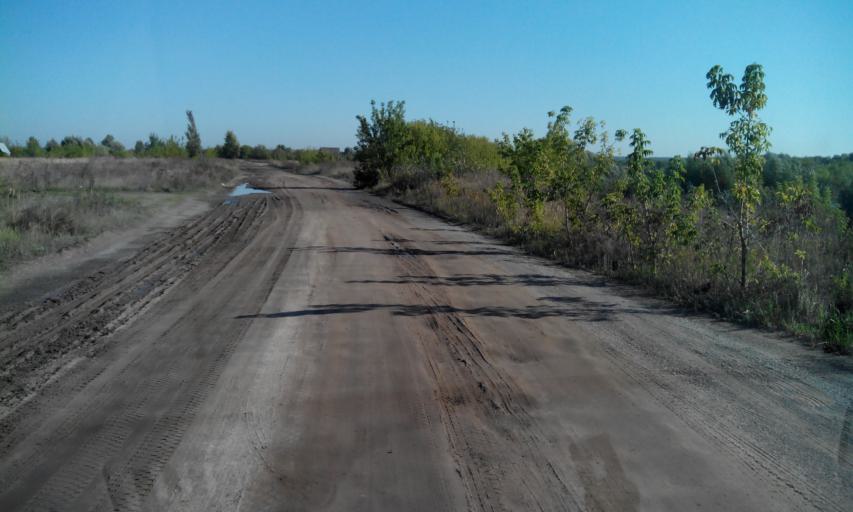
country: RU
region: Penza
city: Bessonovka
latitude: 53.2878
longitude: 45.0611
